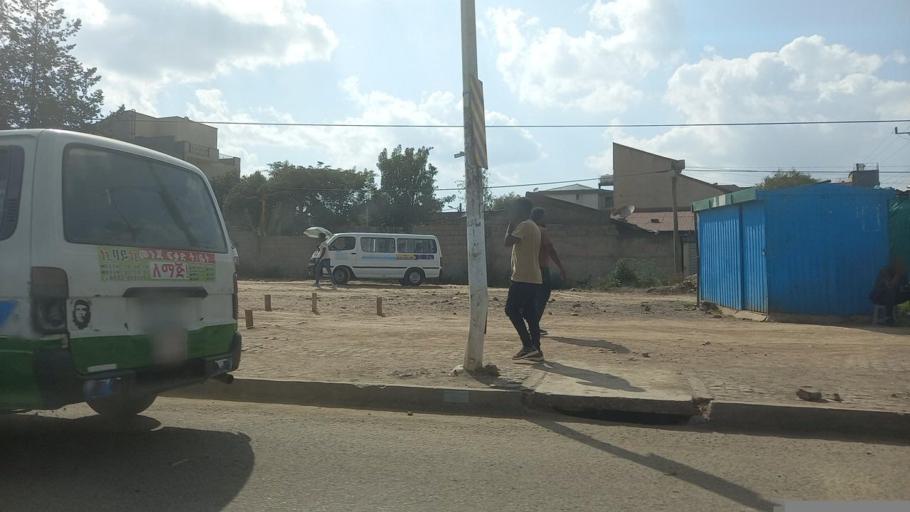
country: ET
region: Adis Abeba
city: Addis Ababa
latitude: 8.9956
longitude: 38.6891
